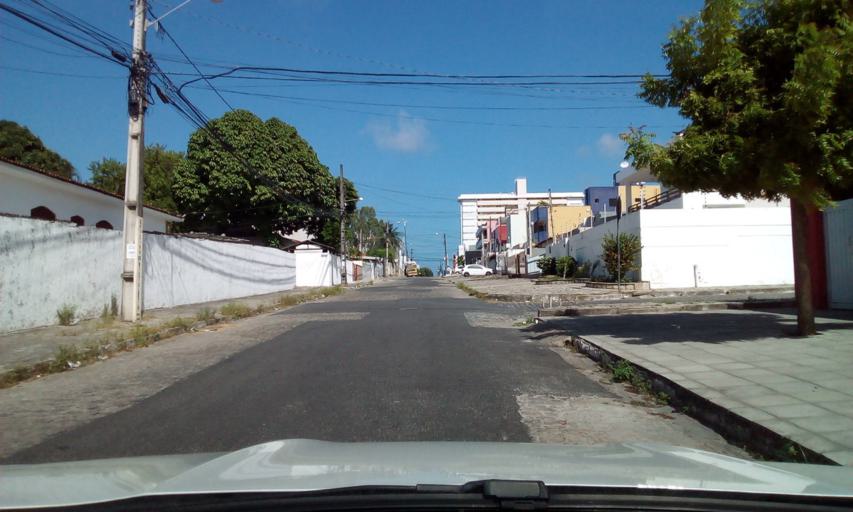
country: BR
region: Paraiba
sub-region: Joao Pessoa
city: Joao Pessoa
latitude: -7.1534
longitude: -34.8405
